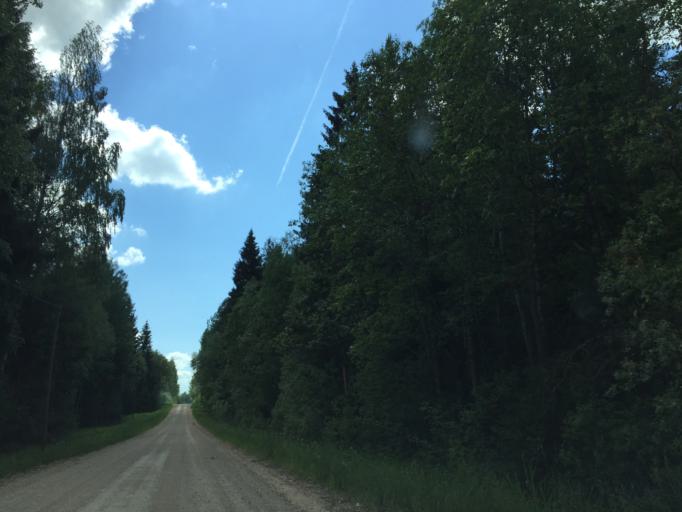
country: LV
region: Priekuli
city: Priekuli
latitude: 57.2316
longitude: 25.4392
